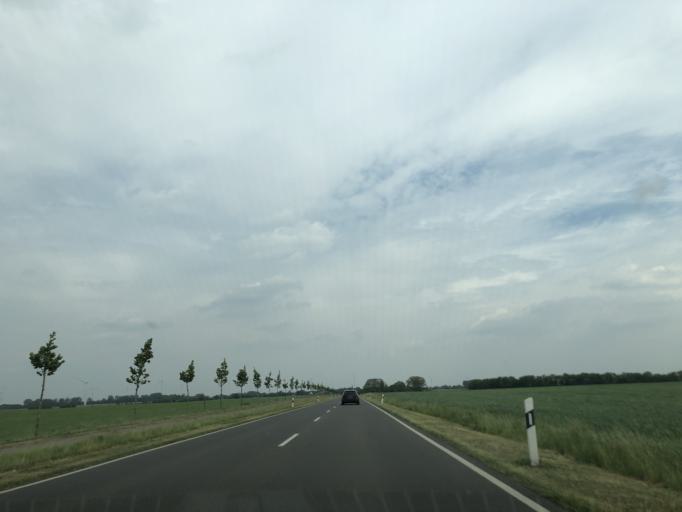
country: DE
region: Brandenburg
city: Dabergotz
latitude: 52.8950
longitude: 12.6950
